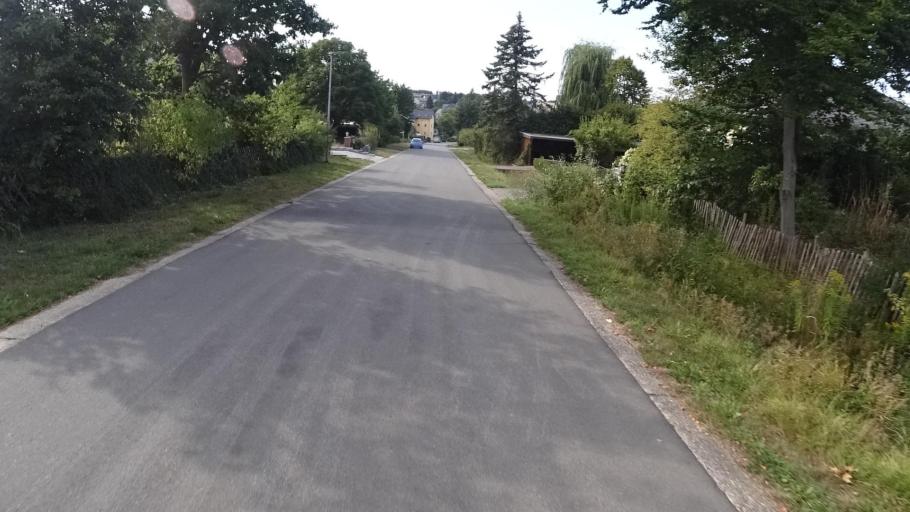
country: DE
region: Rheinland-Pfalz
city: Dichtelbach
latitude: 50.0072
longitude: 7.7012
